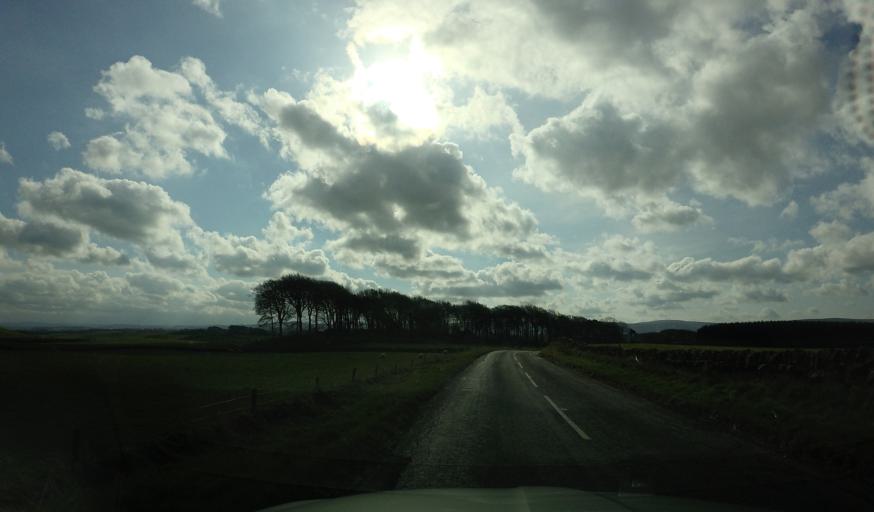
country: GB
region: Scotland
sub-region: Midlothian
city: Penicuik
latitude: 55.8042
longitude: -3.1741
